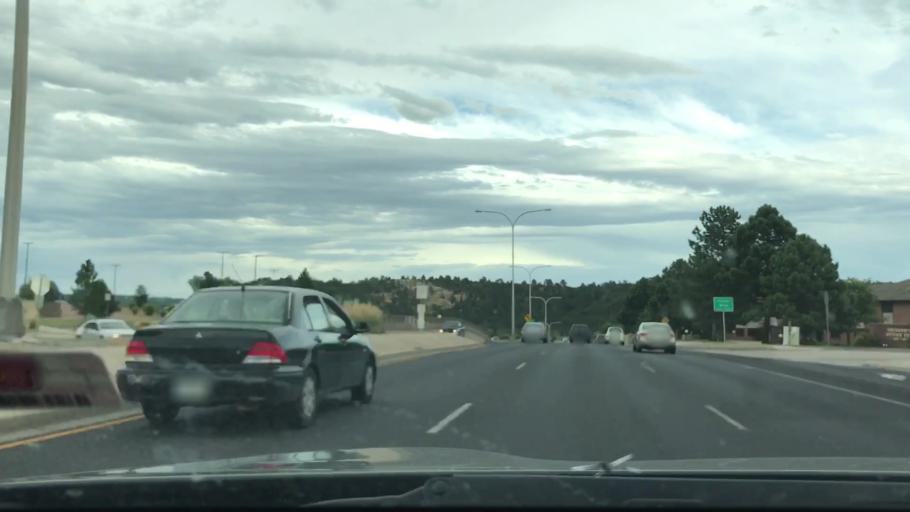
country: US
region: Colorado
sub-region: El Paso County
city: Colorado Springs
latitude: 38.8885
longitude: -104.7932
